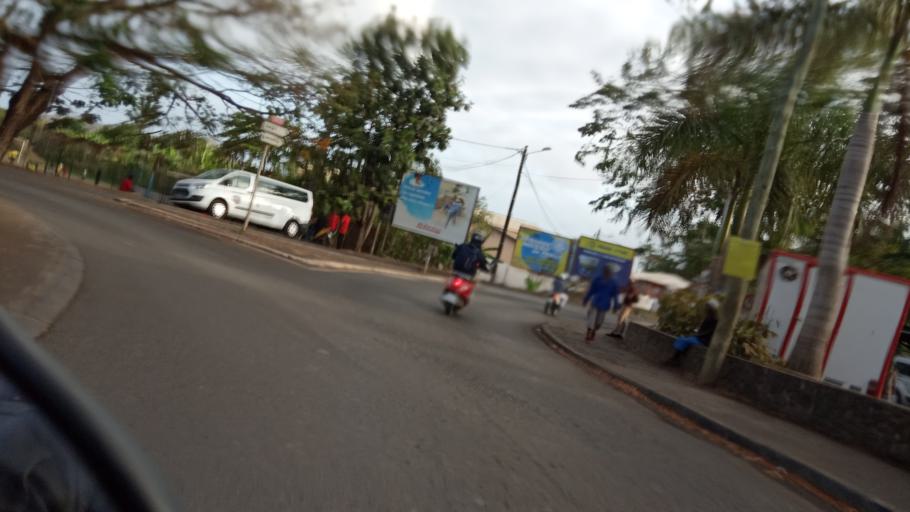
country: YT
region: Mamoudzou
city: Mamoudzou
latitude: -12.7854
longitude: 45.2256
